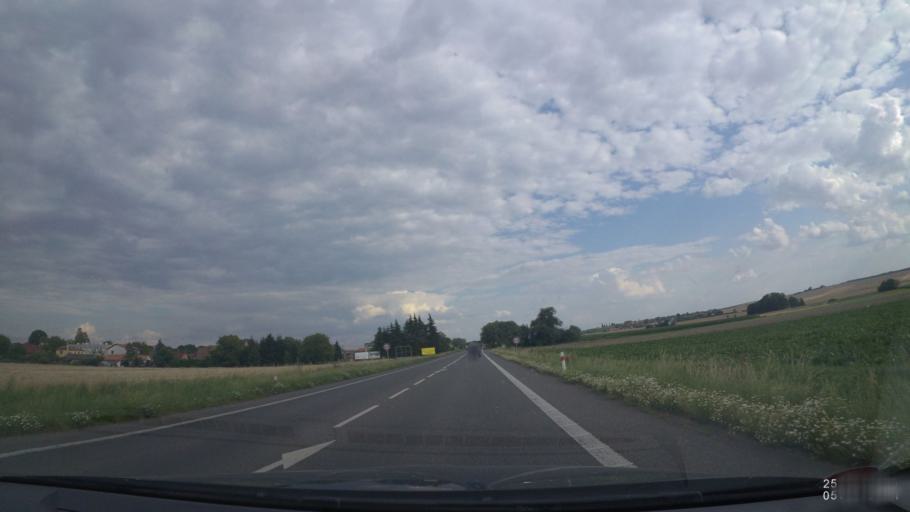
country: CZ
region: Kralovehradecky
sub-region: Okres Hradec Kralove
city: Vsestary
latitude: 50.2650
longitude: 15.7469
